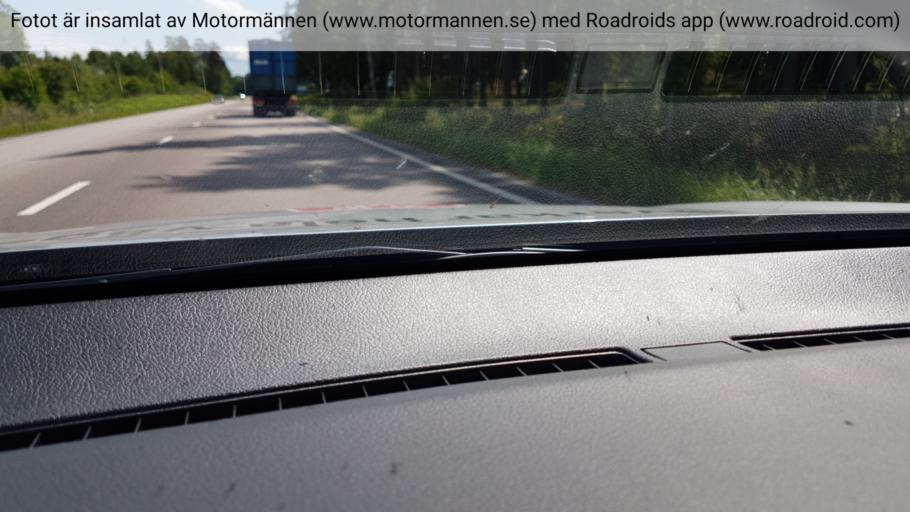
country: SE
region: Vaestra Goetaland
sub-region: Lidkopings Kommun
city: Vinninga
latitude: 58.4244
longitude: 13.3359
